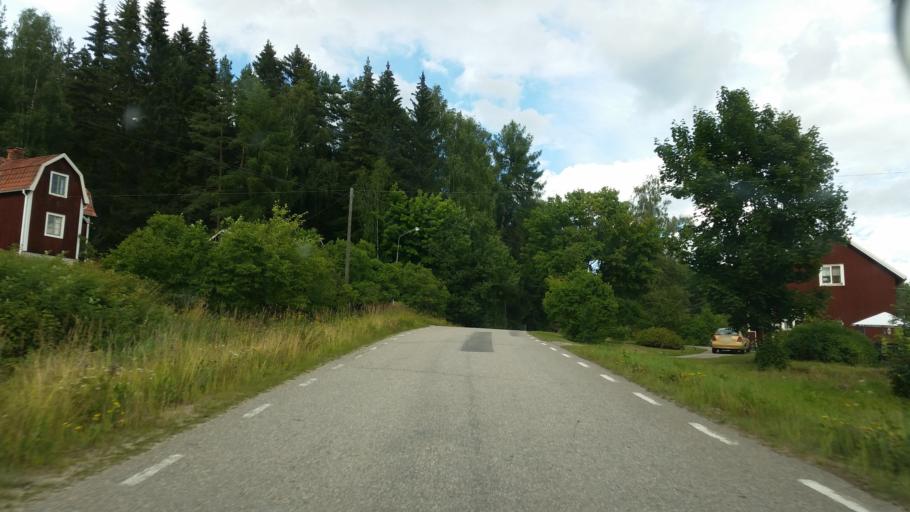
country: SE
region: Gaevleborg
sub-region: Hudiksvalls Kommun
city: Delsbo
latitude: 61.9220
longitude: 16.6149
